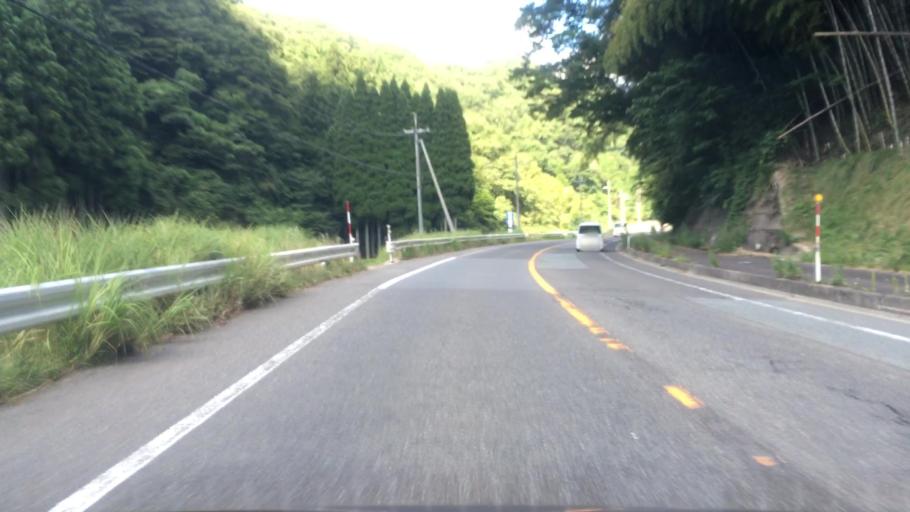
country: JP
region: Hyogo
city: Toyooka
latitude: 35.5761
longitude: 134.7590
